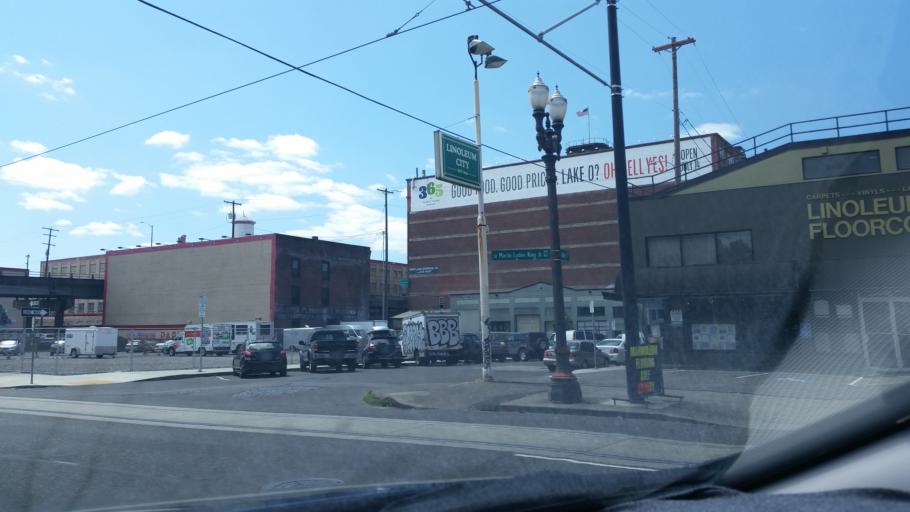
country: US
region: Oregon
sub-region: Multnomah County
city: Portland
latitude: 45.5182
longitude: -122.6617
